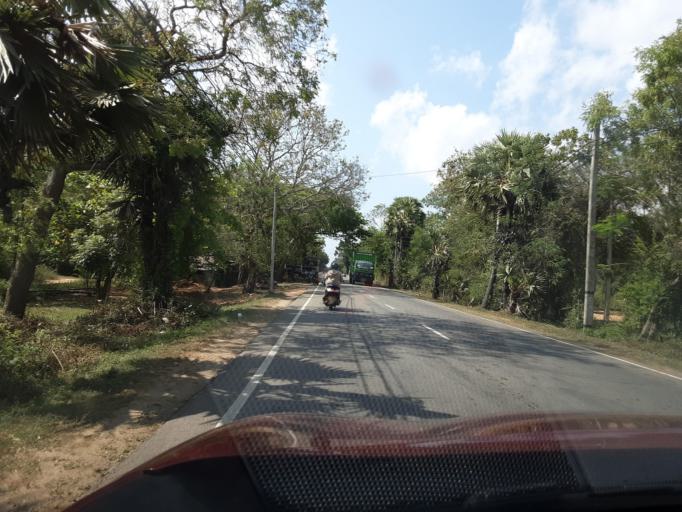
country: LK
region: Southern
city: Tangalla
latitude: 6.2582
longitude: 81.2267
